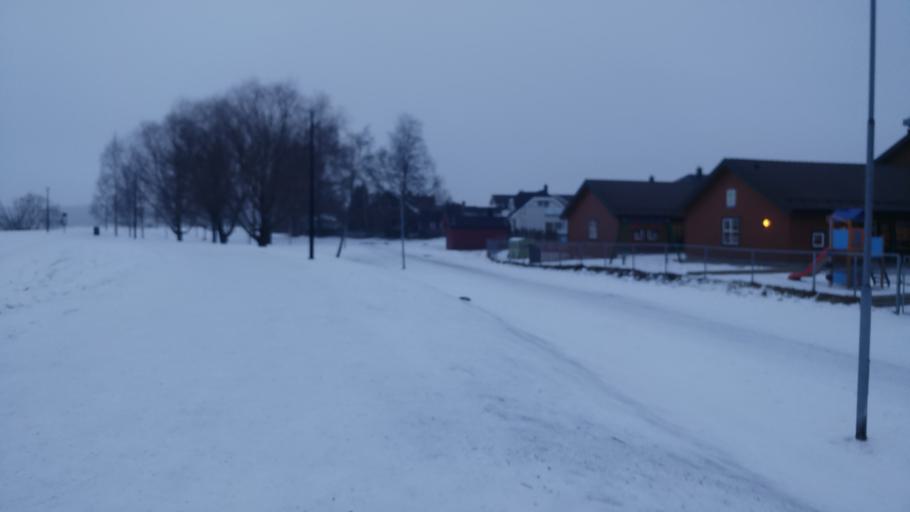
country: NO
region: Akershus
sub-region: Skedsmo
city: Lillestrom
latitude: 59.9596
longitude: 11.0298
